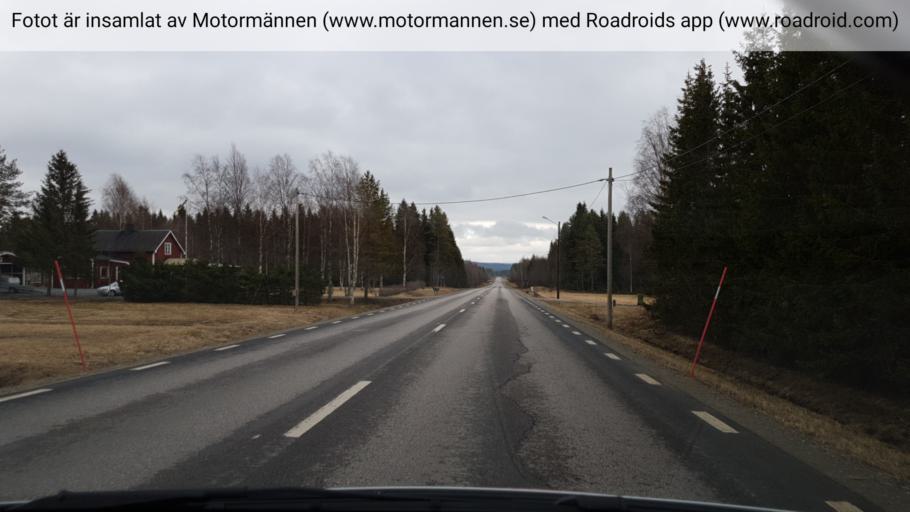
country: SE
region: Vaesterbotten
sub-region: Vannas Kommun
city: Vaennaes
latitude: 63.9144
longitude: 19.6531
